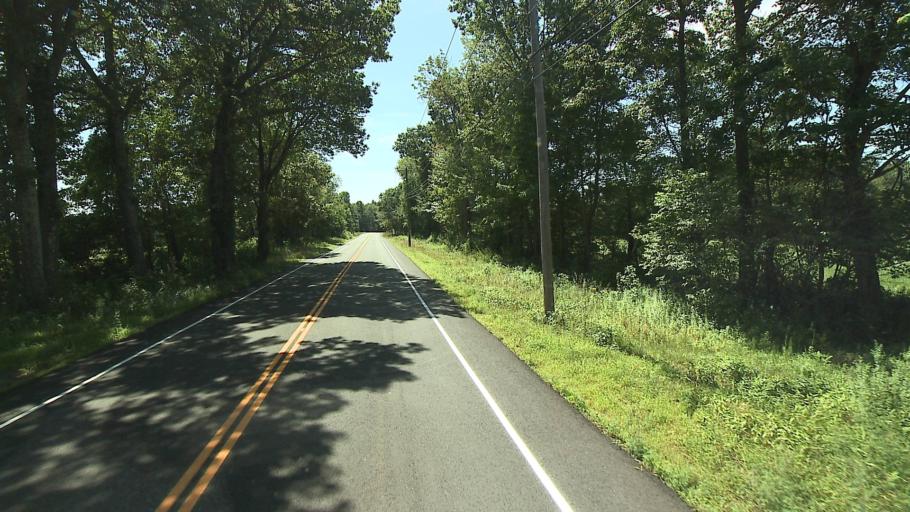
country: US
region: Connecticut
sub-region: Hartford County
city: North Granby
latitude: 41.9679
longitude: -72.9165
